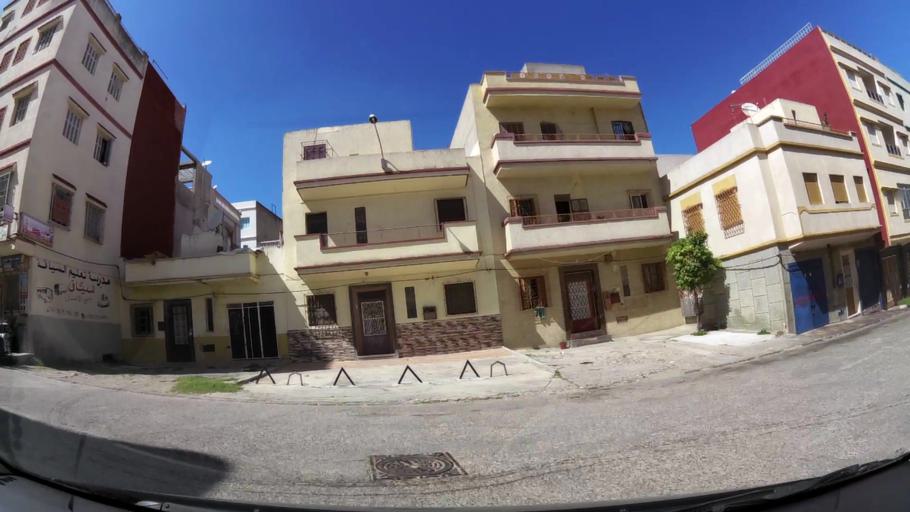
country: MA
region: Tanger-Tetouan
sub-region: Tanger-Assilah
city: Tangier
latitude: 35.7522
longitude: -5.8154
